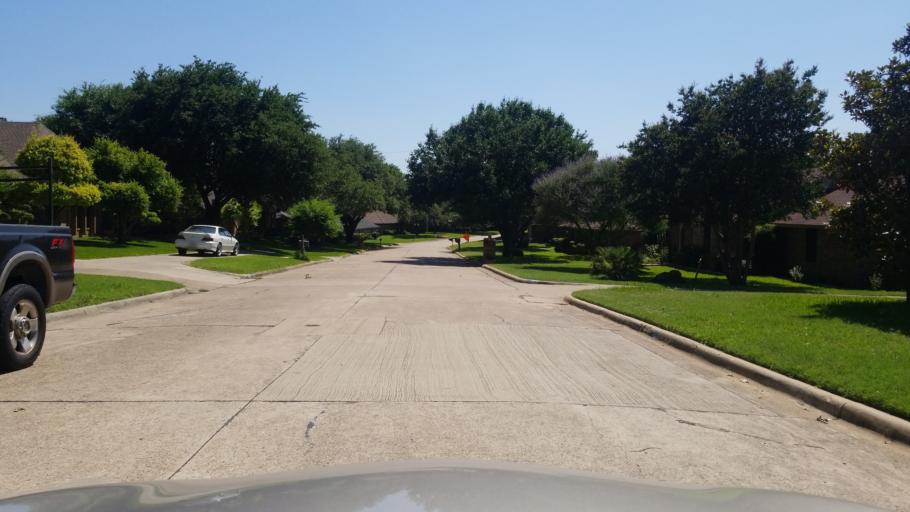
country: US
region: Texas
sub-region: Dallas County
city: Grand Prairie
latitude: 32.6897
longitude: -96.9950
